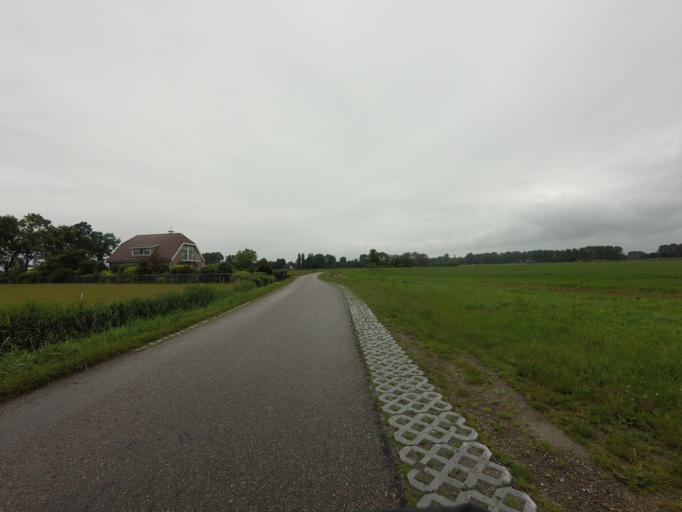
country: NL
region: North Holland
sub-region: Gemeente Schagen
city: Schagen
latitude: 52.7760
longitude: 4.7885
